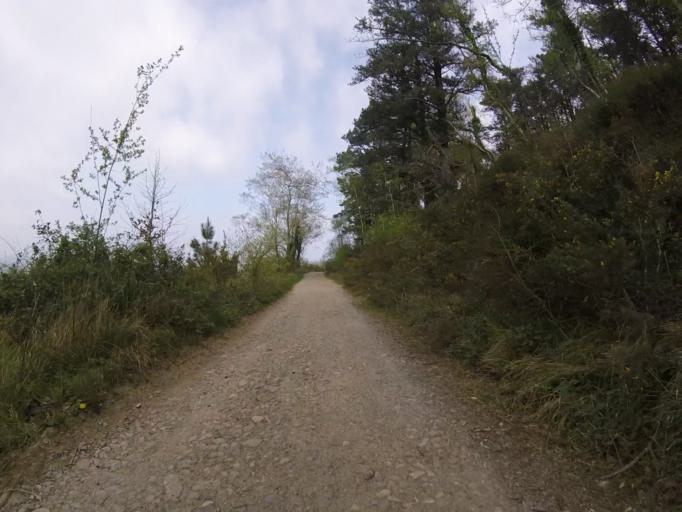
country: ES
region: Basque Country
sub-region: Provincia de Guipuzcoa
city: Usurbil
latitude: 43.2535
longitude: -2.0832
